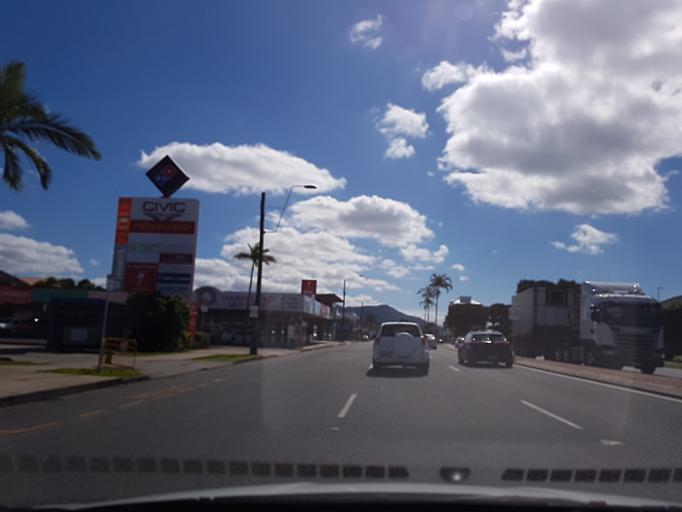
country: AU
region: Queensland
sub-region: Cairns
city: Cairns
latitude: -16.9201
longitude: 145.7706
